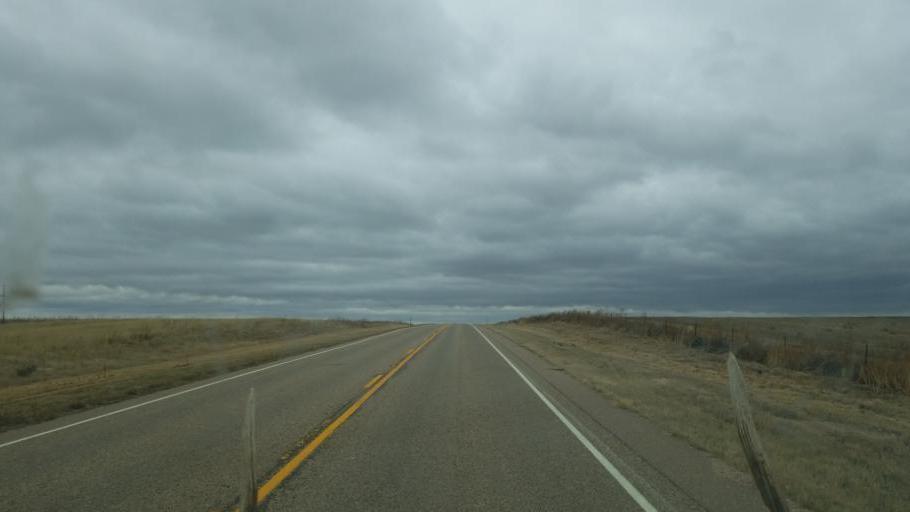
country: US
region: Colorado
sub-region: Cheyenne County
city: Cheyenne Wells
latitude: 38.7980
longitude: -102.6390
